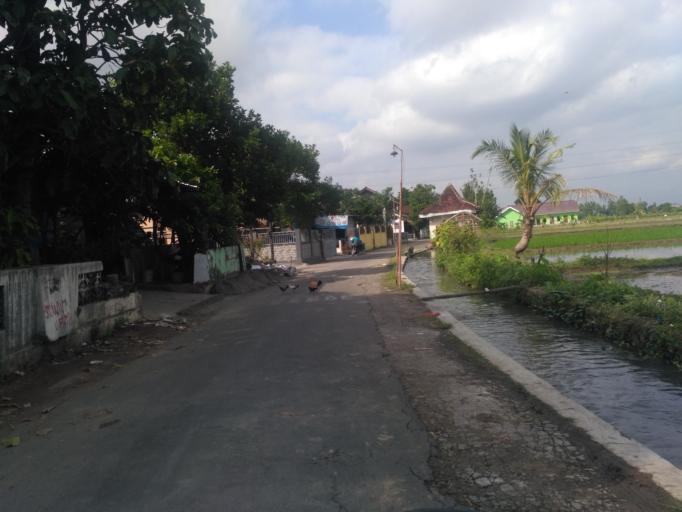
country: ID
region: Daerah Istimewa Yogyakarta
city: Melati
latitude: -7.7570
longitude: 110.3550
